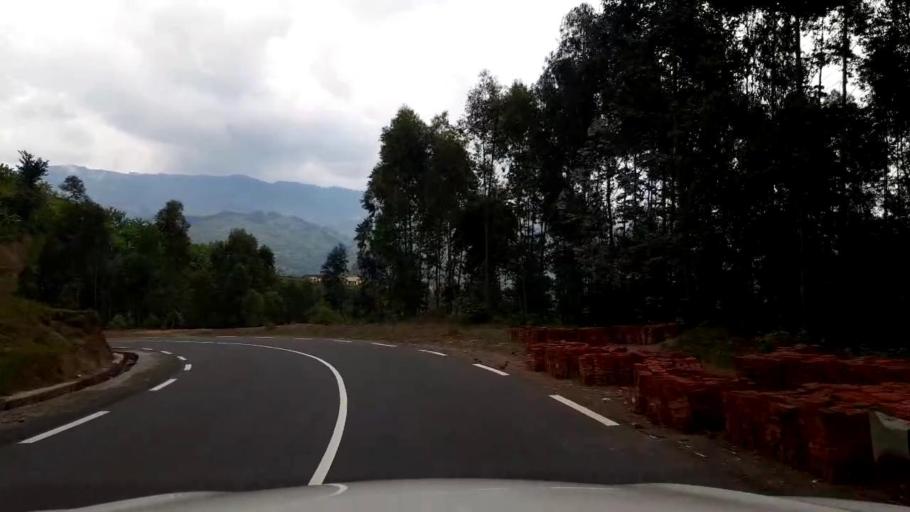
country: RW
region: Western Province
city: Kibuye
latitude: -1.9028
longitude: 29.3602
